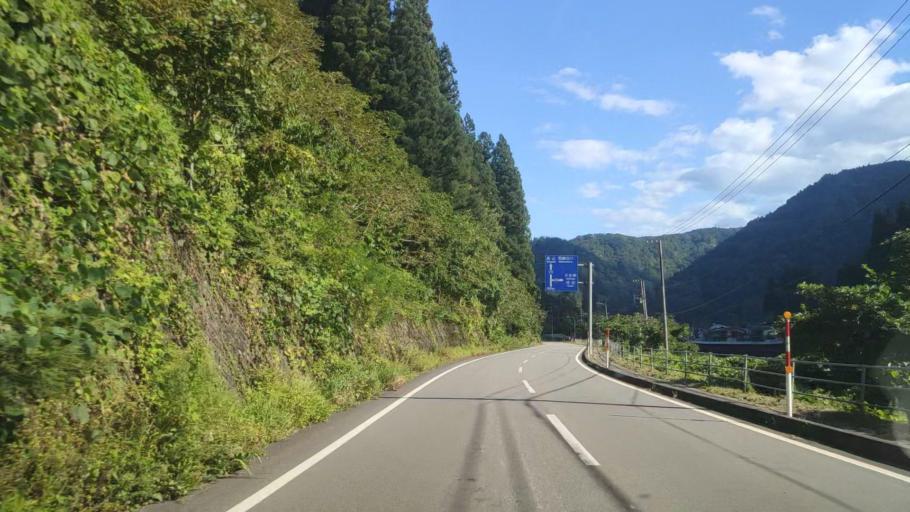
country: JP
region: Gifu
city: Takayama
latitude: 36.3051
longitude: 137.1109
